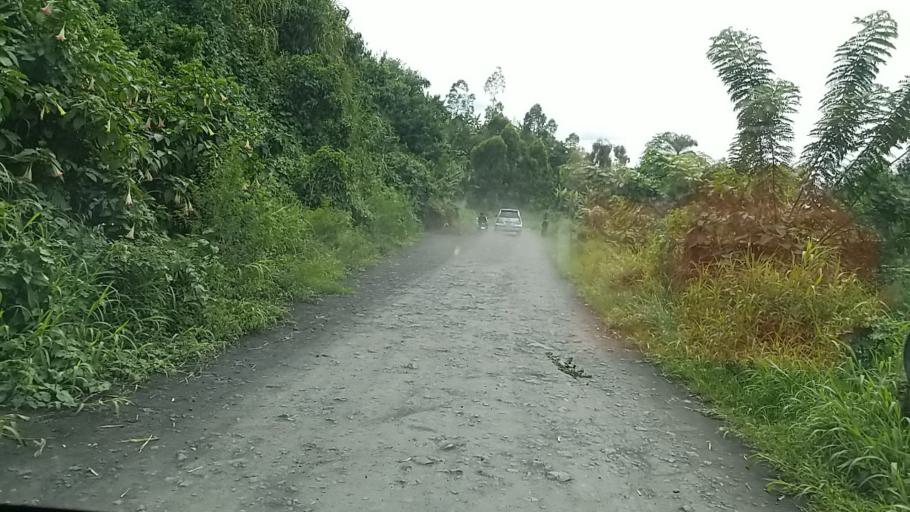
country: CD
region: Nord Kivu
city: Sake
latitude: -1.7380
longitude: 29.0052
